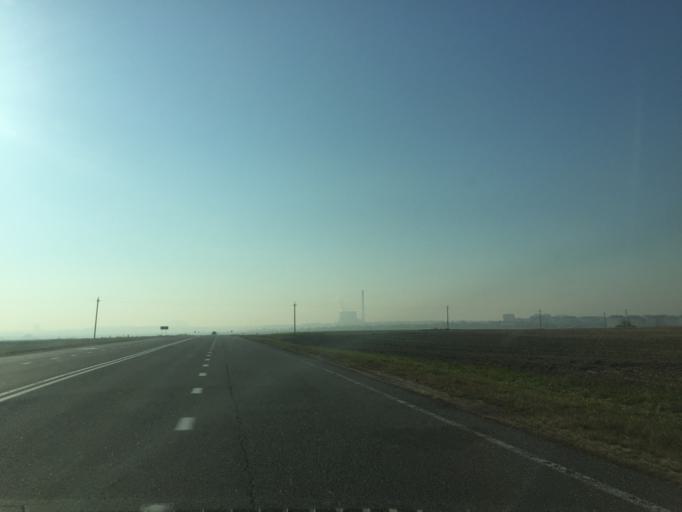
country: BY
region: Gomel
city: Kastsyukowka
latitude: 52.4789
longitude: 30.8212
